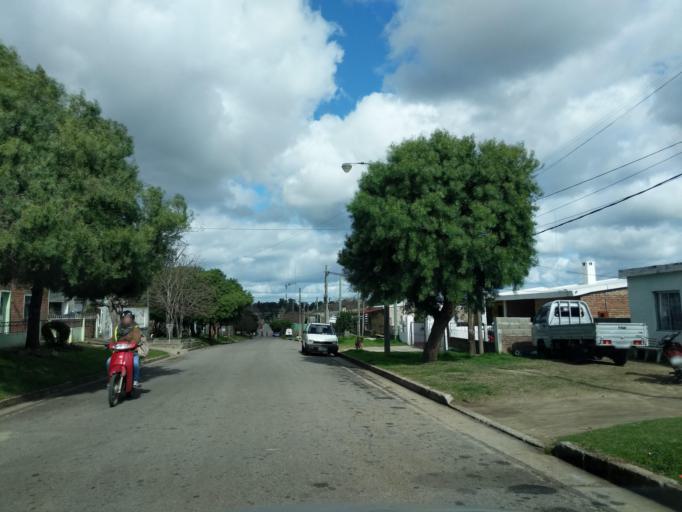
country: UY
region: Florida
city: Florida
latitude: -34.0891
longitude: -56.2300
